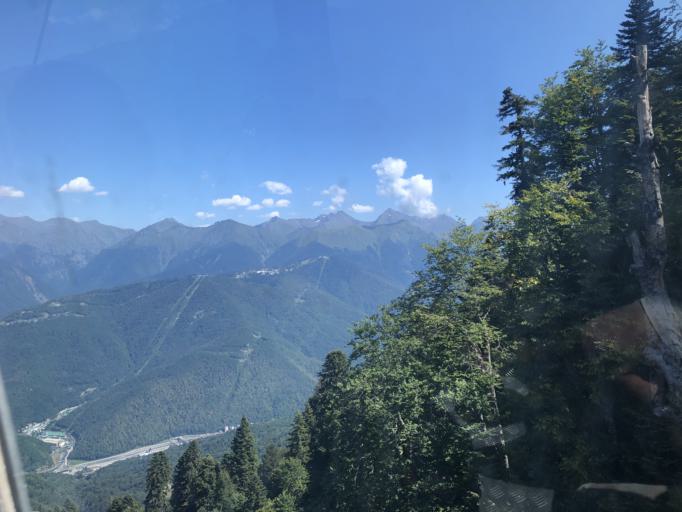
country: RU
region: Krasnodarskiy
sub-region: Sochi City
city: Krasnaya Polyana
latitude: 43.6573
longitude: 40.2515
